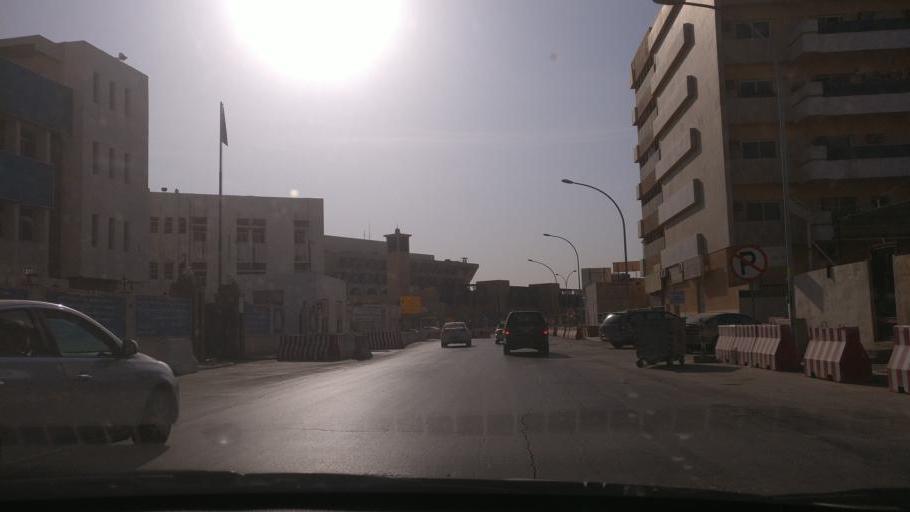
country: SA
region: Ar Riyad
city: Riyadh
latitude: 24.6605
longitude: 46.7036
